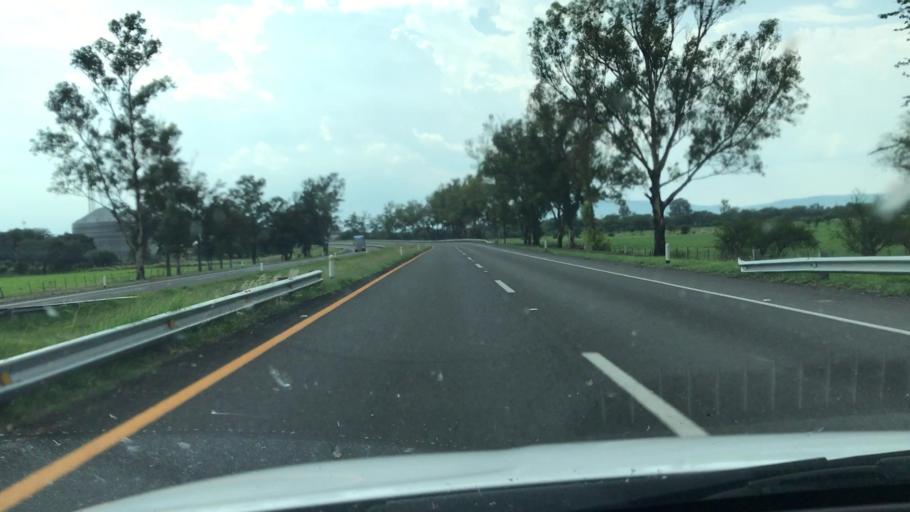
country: MX
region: Jalisco
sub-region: Ocotlan
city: Joconoxtle (La Tuna)
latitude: 20.3706
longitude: -102.6562
